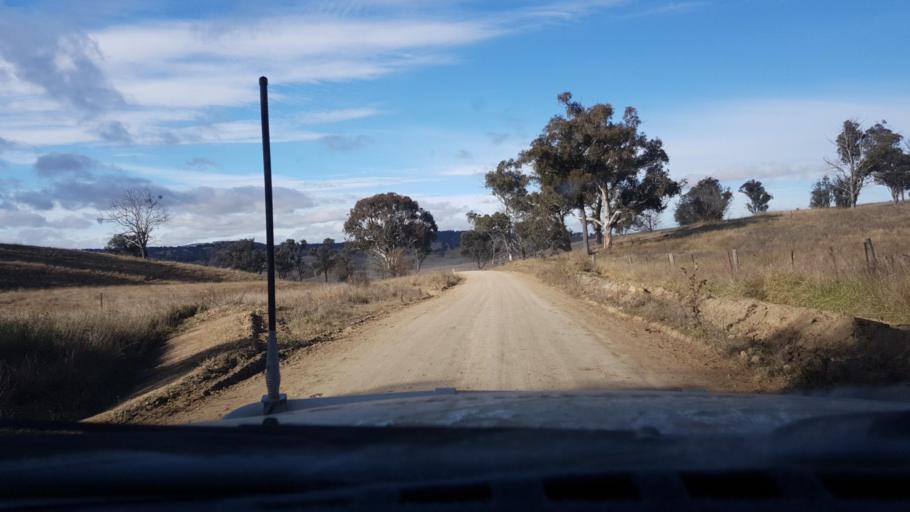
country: AU
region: New South Wales
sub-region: Armidale Dumaresq
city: Enmore
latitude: -30.7601
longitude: 151.6316
